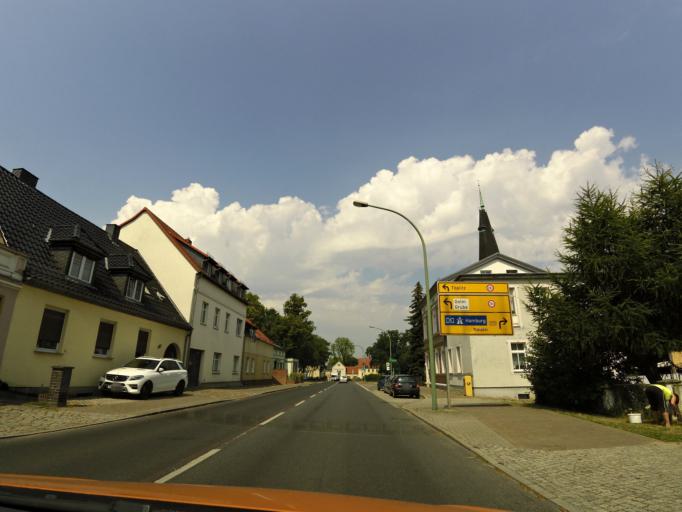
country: DE
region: Brandenburg
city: Potsdam
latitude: 52.4230
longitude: 13.0010
